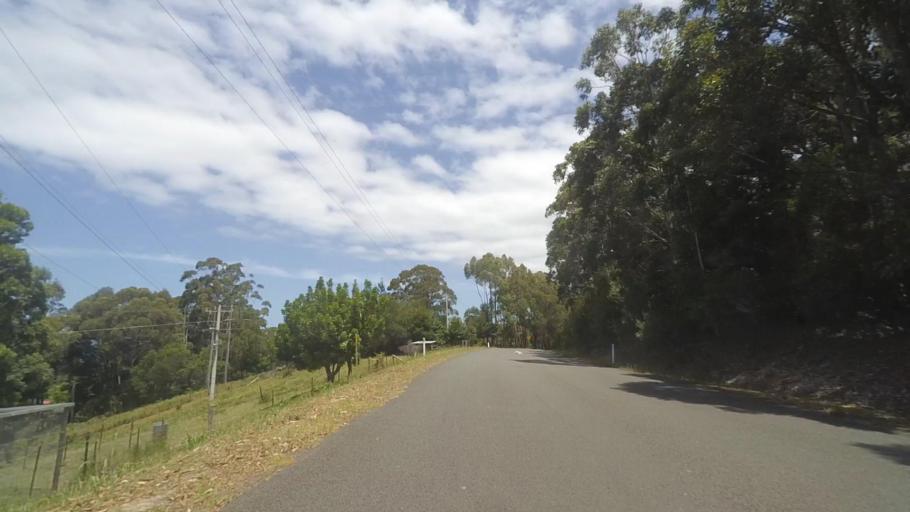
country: AU
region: New South Wales
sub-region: Shoalhaven Shire
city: Milton
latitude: -35.3964
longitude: 150.3689
